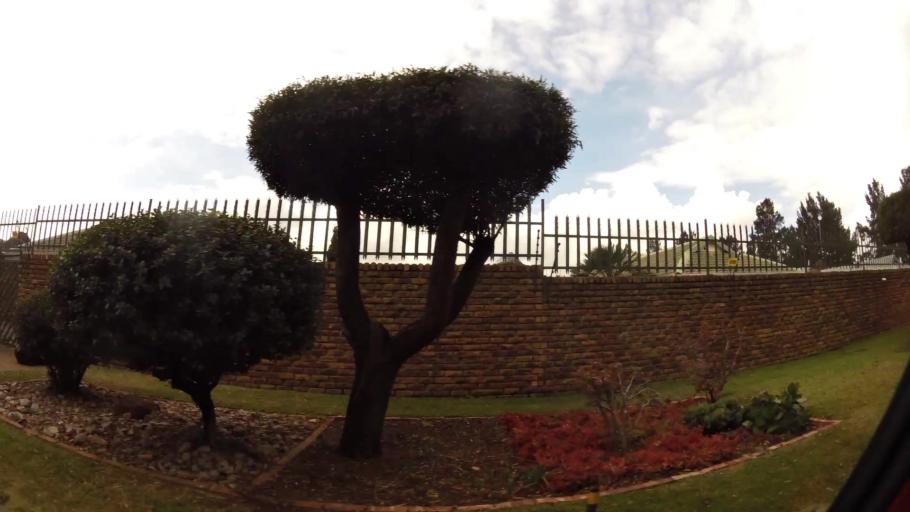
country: ZA
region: Gauteng
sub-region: Sedibeng District Municipality
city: Vanderbijlpark
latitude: -26.7379
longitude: 27.8492
